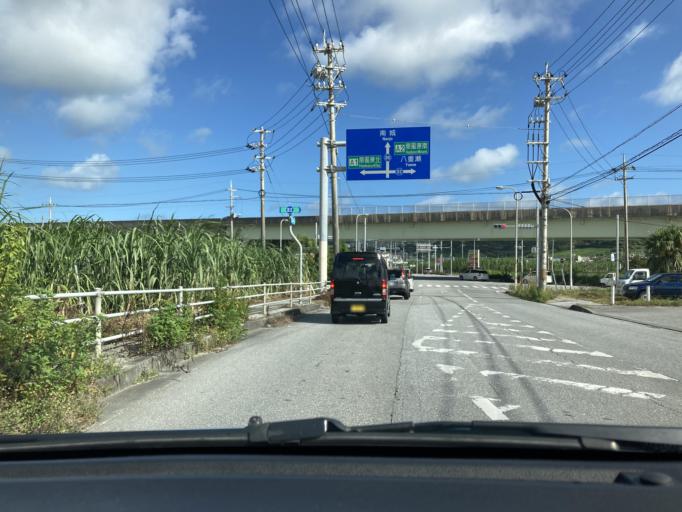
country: JP
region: Okinawa
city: Tomigusuku
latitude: 26.1839
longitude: 127.7336
